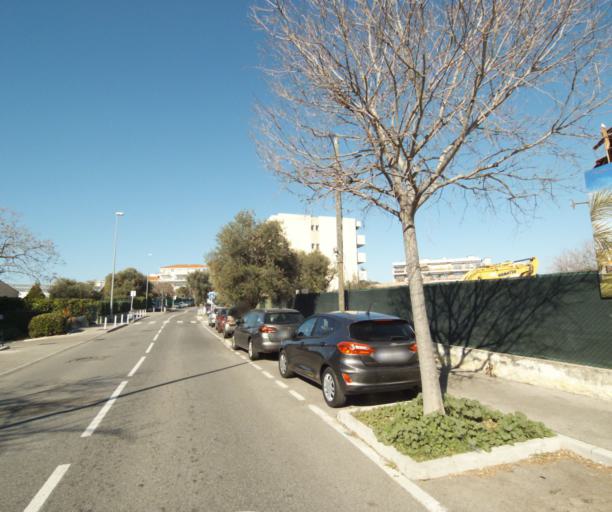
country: FR
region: Provence-Alpes-Cote d'Azur
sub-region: Departement des Alpes-Maritimes
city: Biot
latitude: 43.5953
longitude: 7.1002
